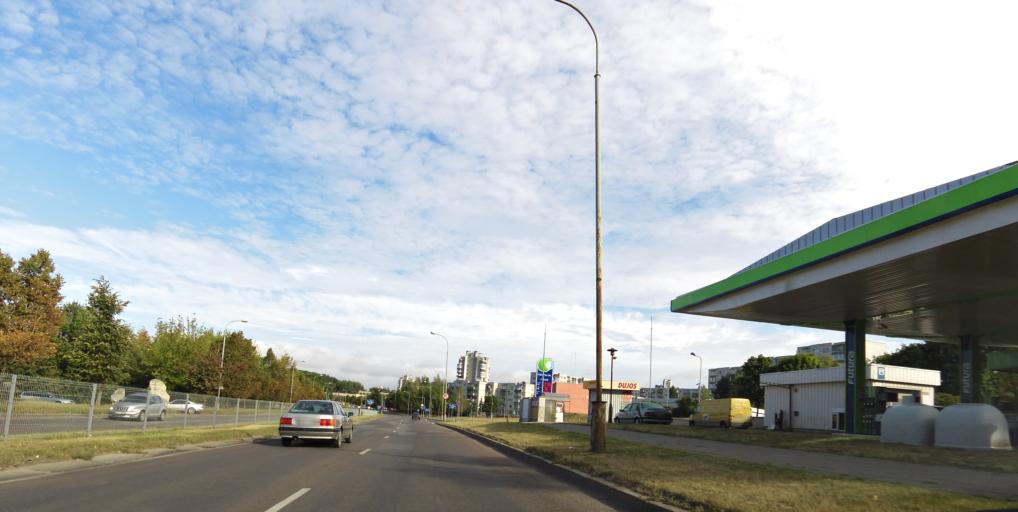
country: LT
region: Vilnius County
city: Seskine
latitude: 54.7106
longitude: 25.2400
